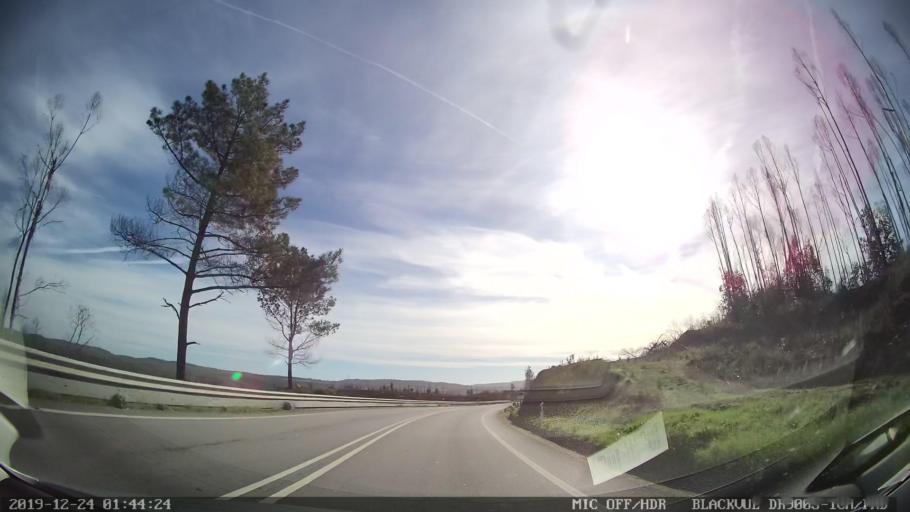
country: PT
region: Portalegre
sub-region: Nisa
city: Nisa
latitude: 39.5554
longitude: -7.7942
